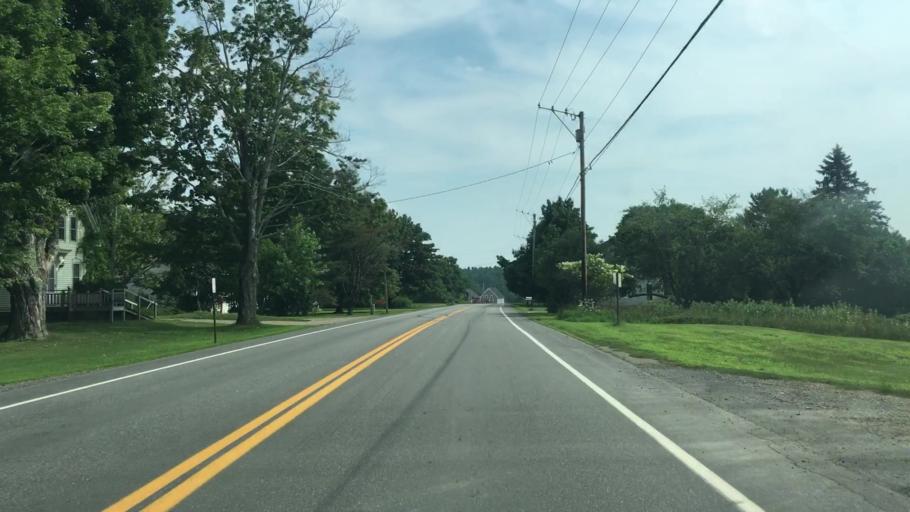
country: US
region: Maine
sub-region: Kennebec County
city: Windsor
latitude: 44.3092
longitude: -69.5808
